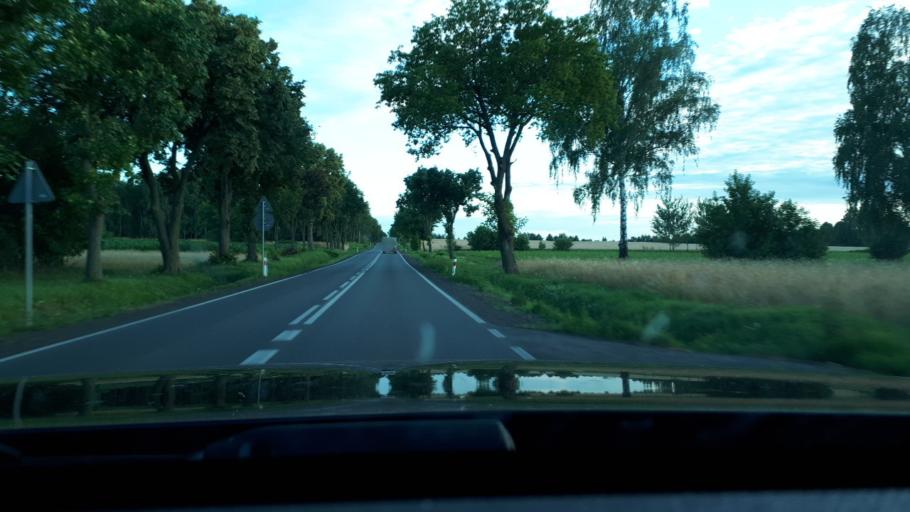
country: PL
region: Masovian Voivodeship
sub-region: Powiat ciechanowski
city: Ojrzen
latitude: 52.7455
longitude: 20.5276
